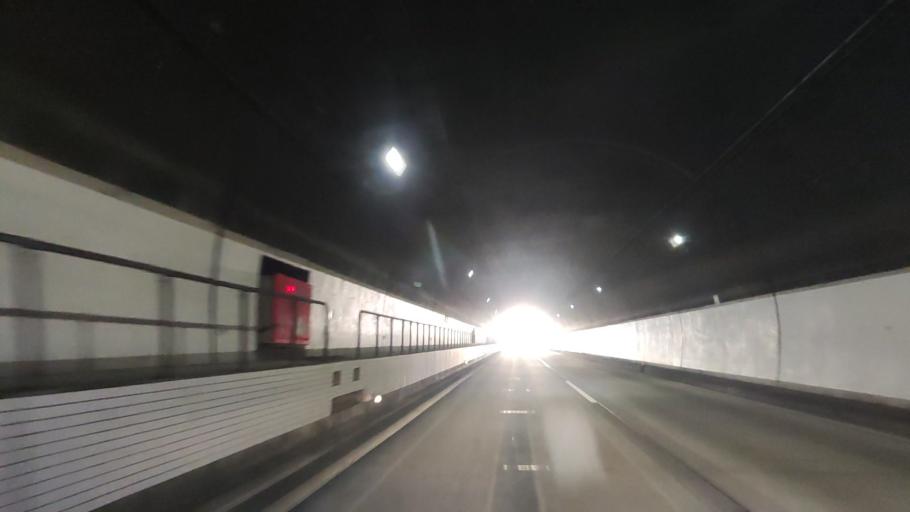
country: JP
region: Ehime
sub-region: Shikoku-chuo Shi
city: Matsuyama
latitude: 33.8196
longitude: 132.9636
